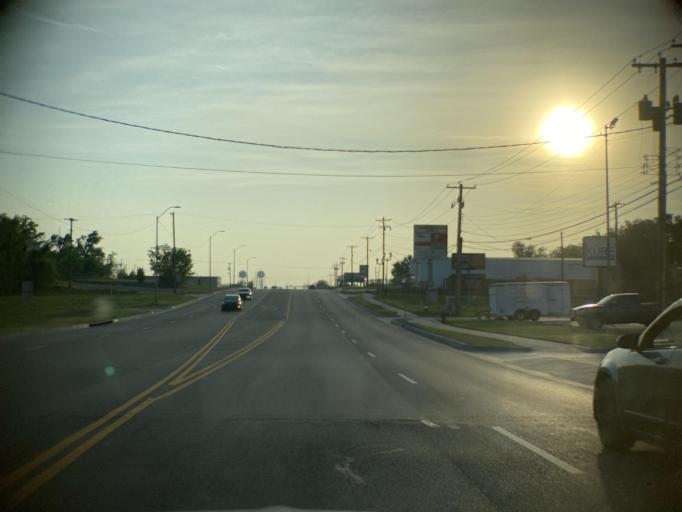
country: US
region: Oklahoma
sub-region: Oklahoma County
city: Midwest City
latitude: 35.4353
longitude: -97.3714
